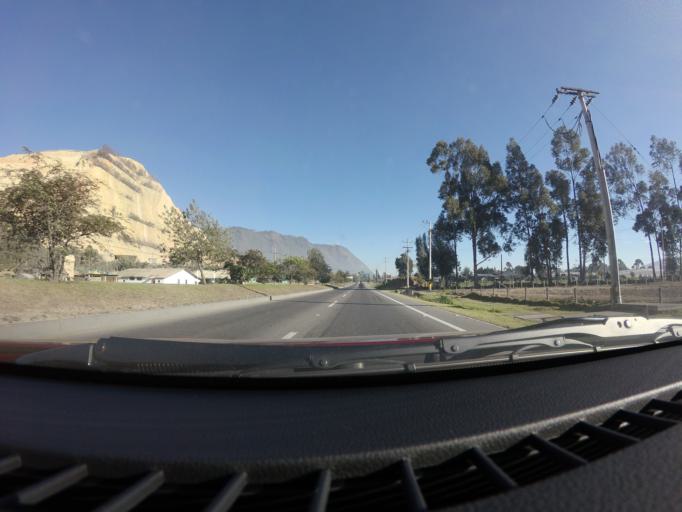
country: CO
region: Cundinamarca
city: Cajica
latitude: 4.9523
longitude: -74.0142
